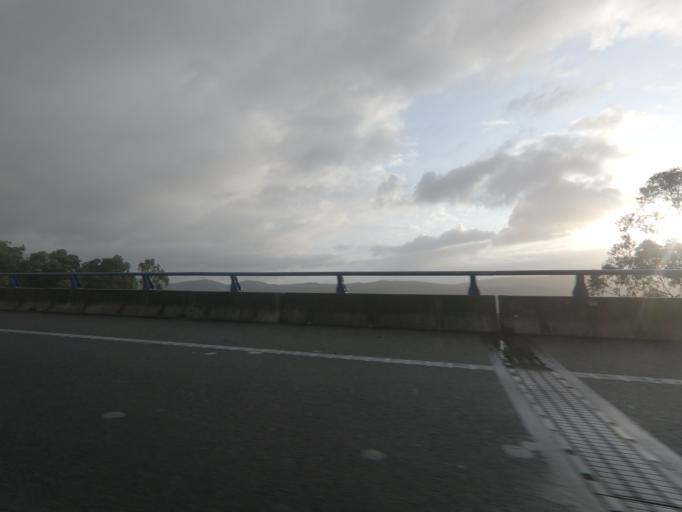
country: ES
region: Galicia
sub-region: Provincia de Pontevedra
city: Porrino
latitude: 42.1757
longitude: -8.6500
